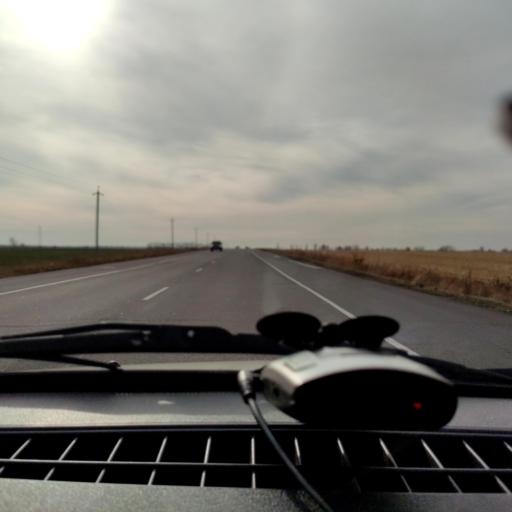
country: RU
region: Voronezj
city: Devitsa
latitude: 51.5685
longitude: 38.9743
